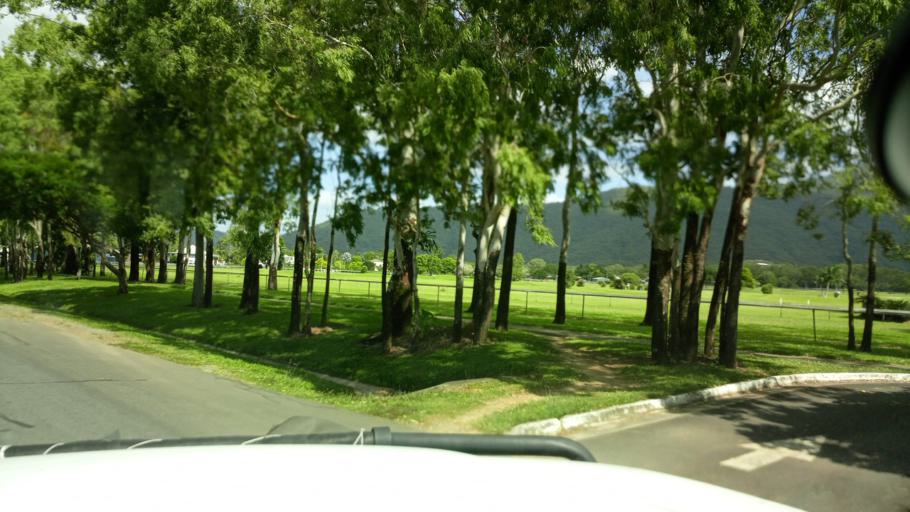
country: AU
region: Queensland
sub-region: Cairns
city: Woree
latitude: -17.0921
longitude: 145.7851
